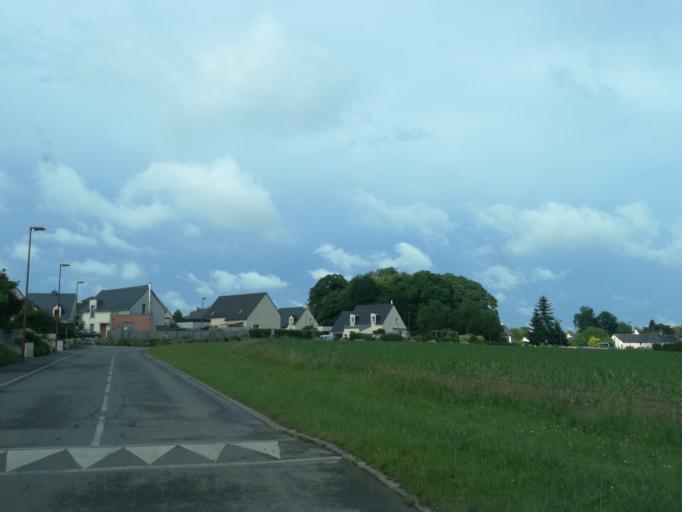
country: FR
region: Brittany
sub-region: Departement d'Ille-et-Vilaine
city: Bedee
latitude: 48.1759
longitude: -1.9478
